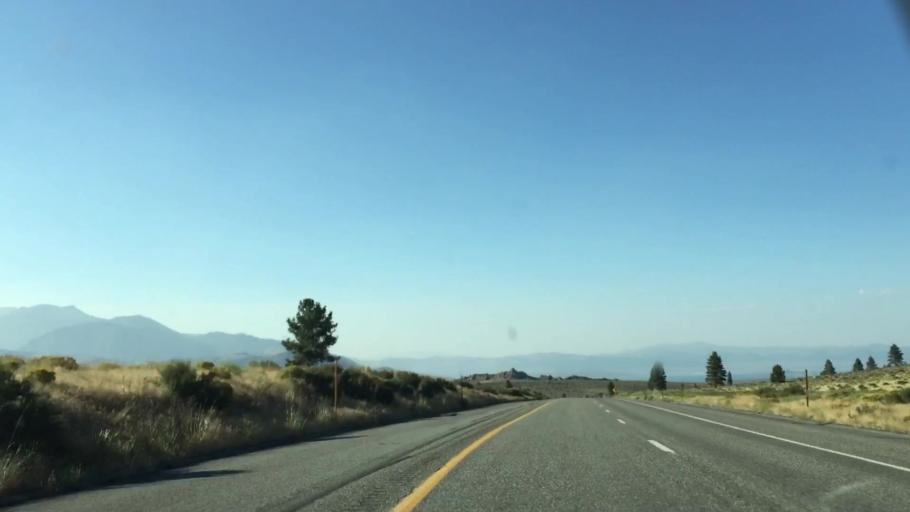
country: US
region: California
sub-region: Mono County
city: Mammoth Lakes
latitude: 37.8343
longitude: -119.0695
